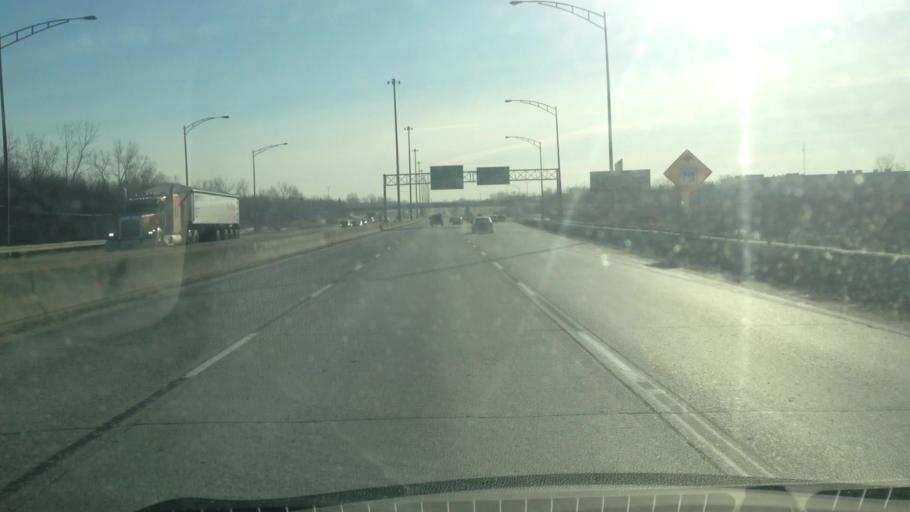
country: CA
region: Quebec
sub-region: Laurentides
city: Boisbriand
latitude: 45.5778
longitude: -73.8345
